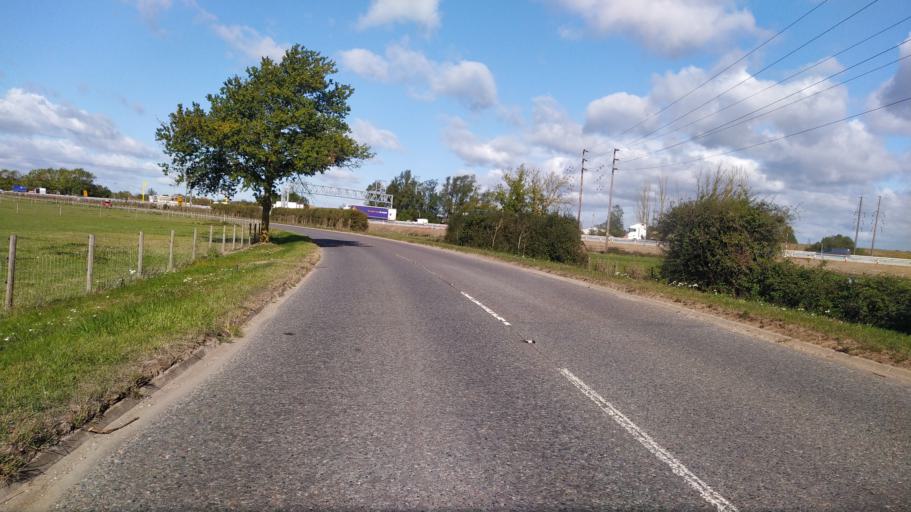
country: GB
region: England
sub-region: West Berkshire
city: Calcot
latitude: 51.4201
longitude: -1.0194
